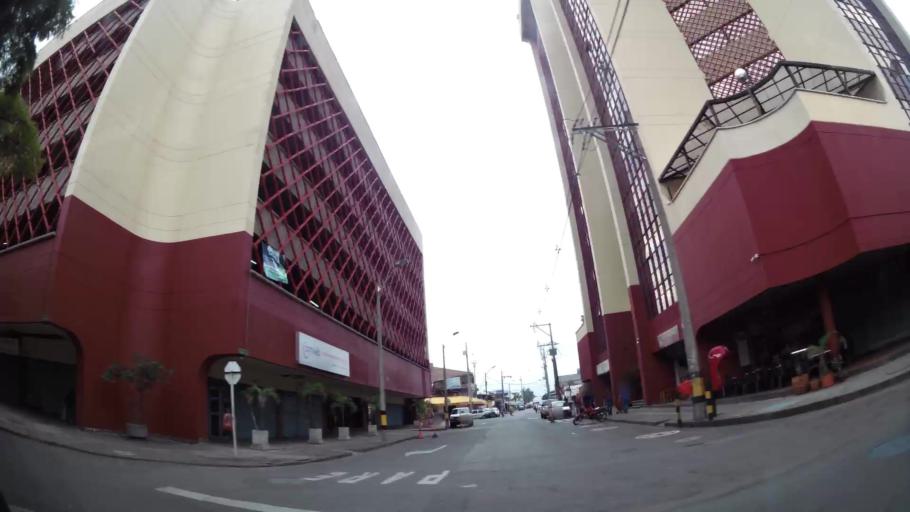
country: CO
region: Antioquia
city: Medellin
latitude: 6.2424
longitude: -75.5748
